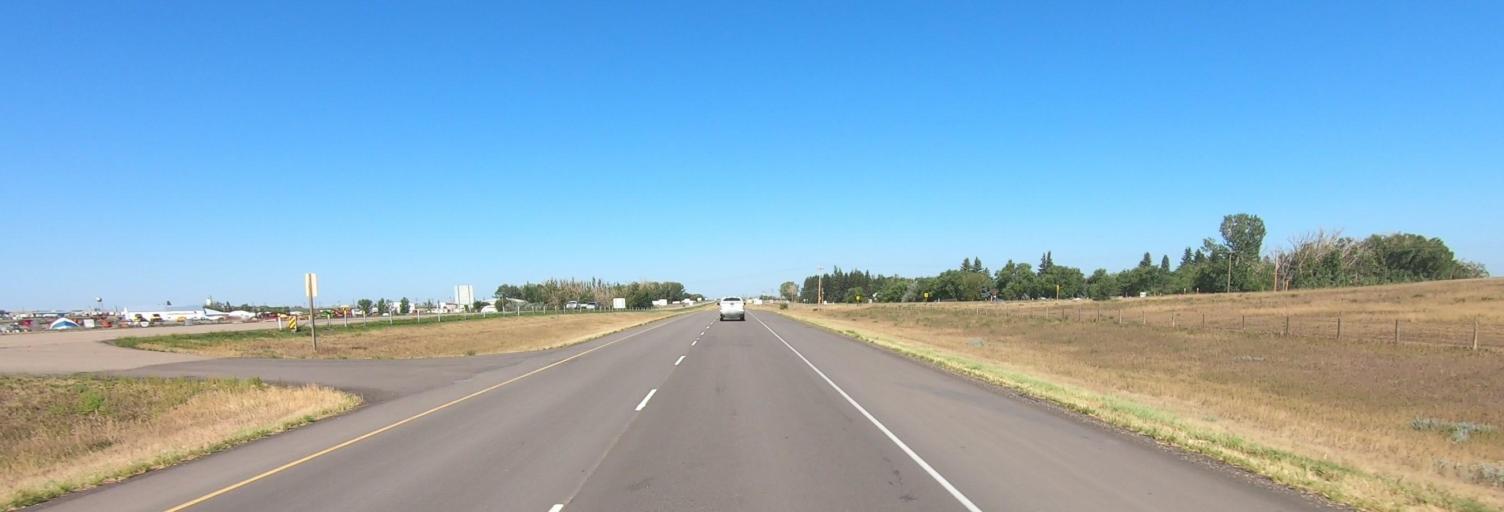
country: CA
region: Alberta
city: Brooks
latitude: 50.5998
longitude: -111.9138
